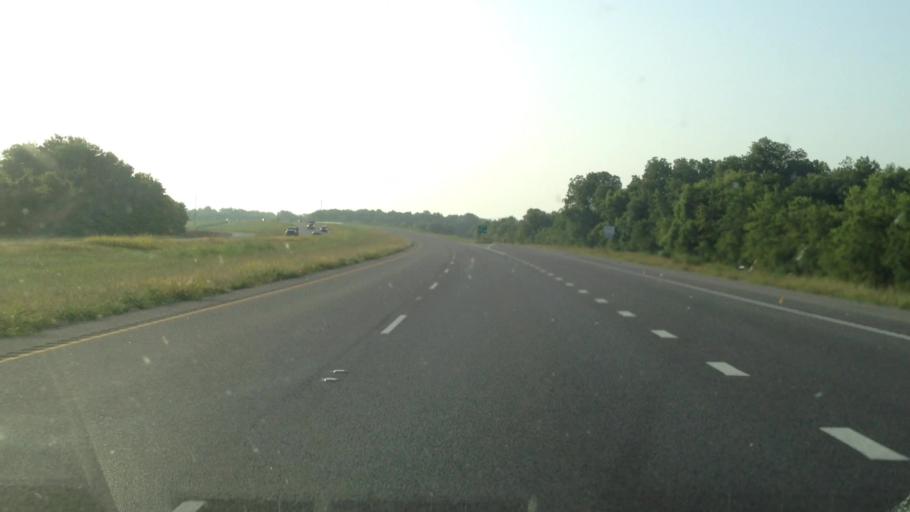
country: US
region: Louisiana
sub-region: Rapides Parish
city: Boyce
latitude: 31.3813
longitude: -92.6767
